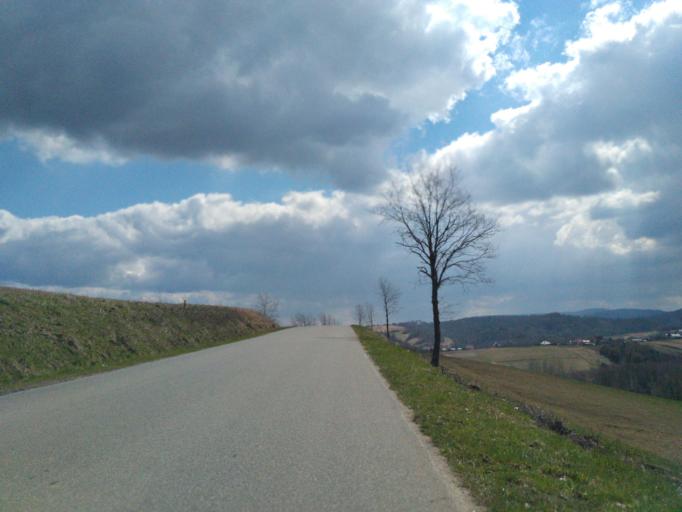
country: PL
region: Subcarpathian Voivodeship
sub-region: Powiat brzozowski
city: Dydnia
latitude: 49.6539
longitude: 22.2093
